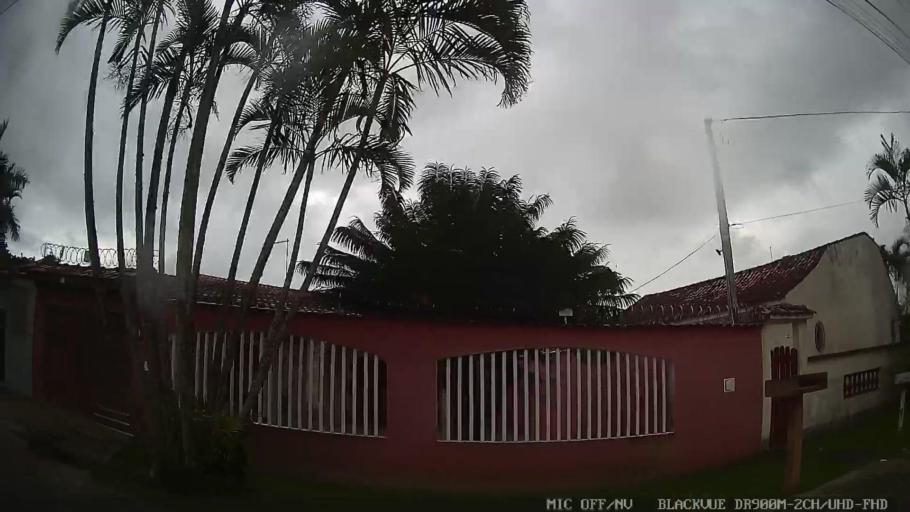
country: BR
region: Sao Paulo
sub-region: Itanhaem
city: Itanhaem
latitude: -24.1409
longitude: -46.7096
